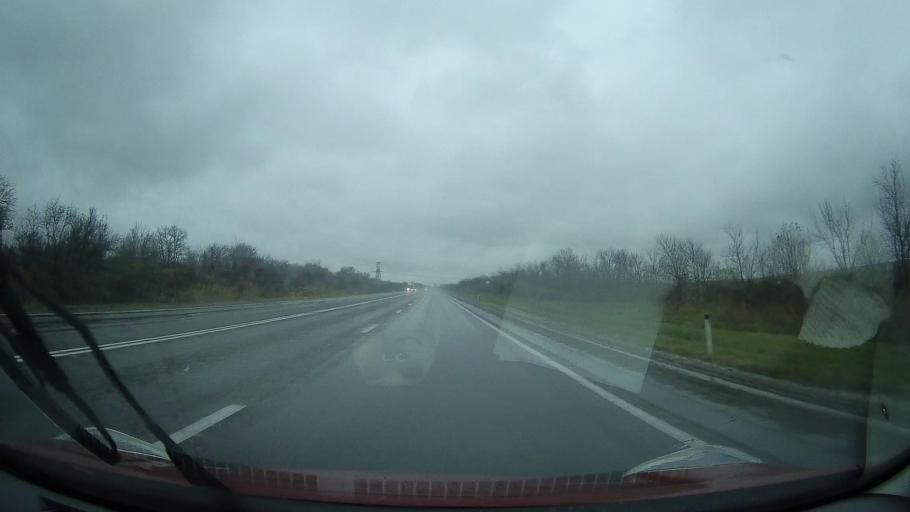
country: RU
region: Stavropol'skiy
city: Nevinnomyssk
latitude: 44.6331
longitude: 42.0137
